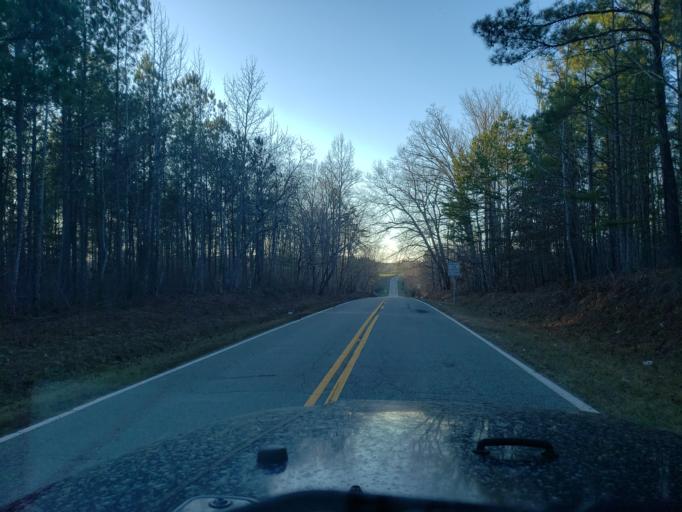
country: US
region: South Carolina
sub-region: Cherokee County
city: Blacksburg
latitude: 35.0491
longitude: -81.4164
